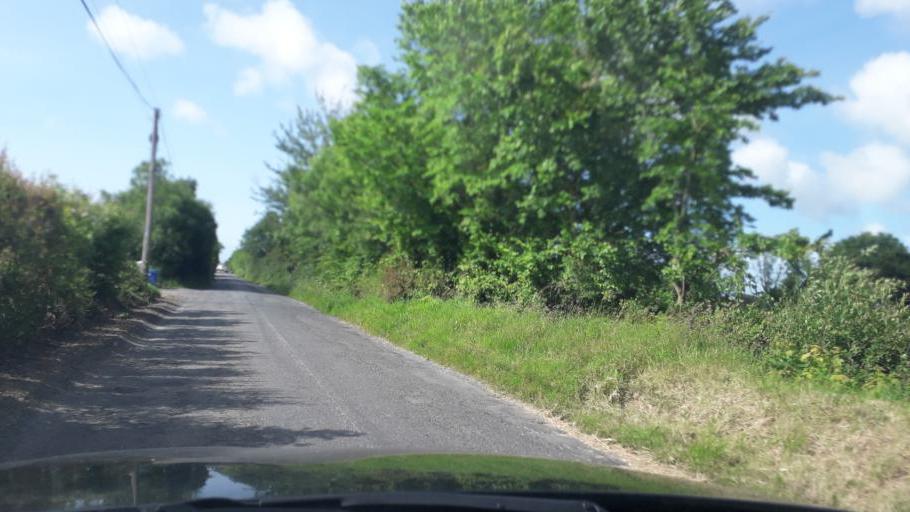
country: IE
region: Leinster
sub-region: Loch Garman
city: Loch Garman
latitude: 52.2498
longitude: -6.5499
